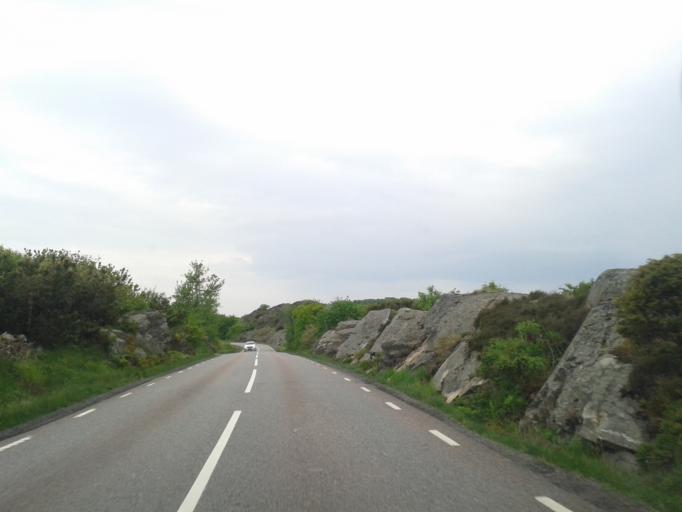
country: SE
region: Vaestra Goetaland
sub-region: Kungalvs Kommun
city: Marstrand
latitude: 57.8941
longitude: 11.7079
